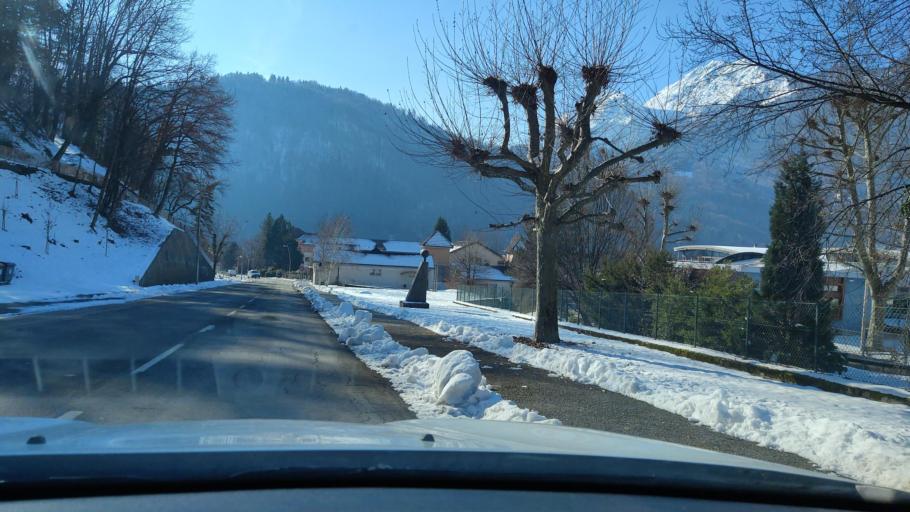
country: FR
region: Rhone-Alpes
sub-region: Departement de la Savoie
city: Ugine
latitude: 45.7531
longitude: 6.4185
